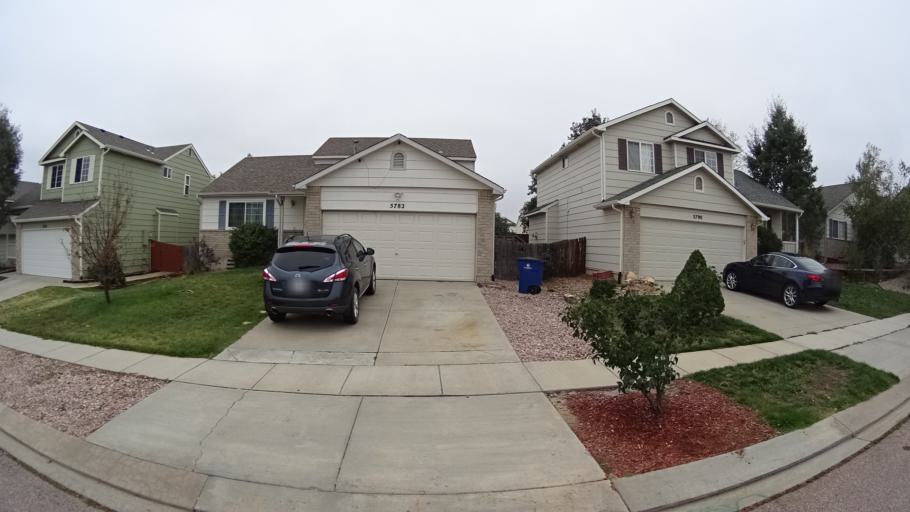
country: US
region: Colorado
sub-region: El Paso County
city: Cimarron Hills
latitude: 38.9158
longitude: -104.7131
